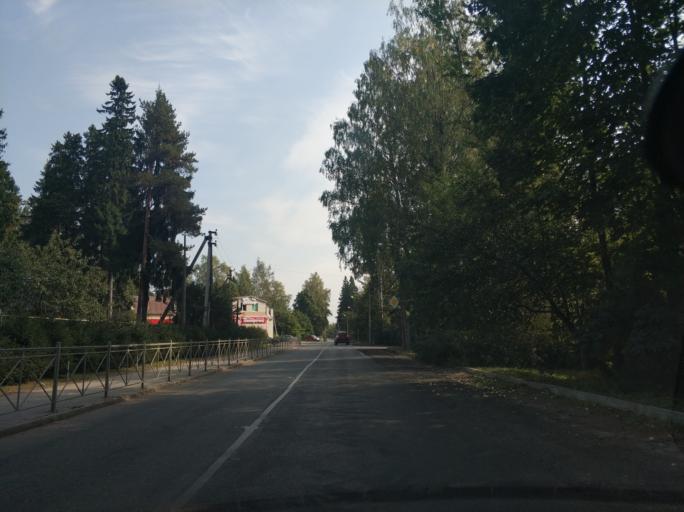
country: RU
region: Leningrad
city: Vsevolozhsk
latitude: 60.0200
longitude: 30.6680
